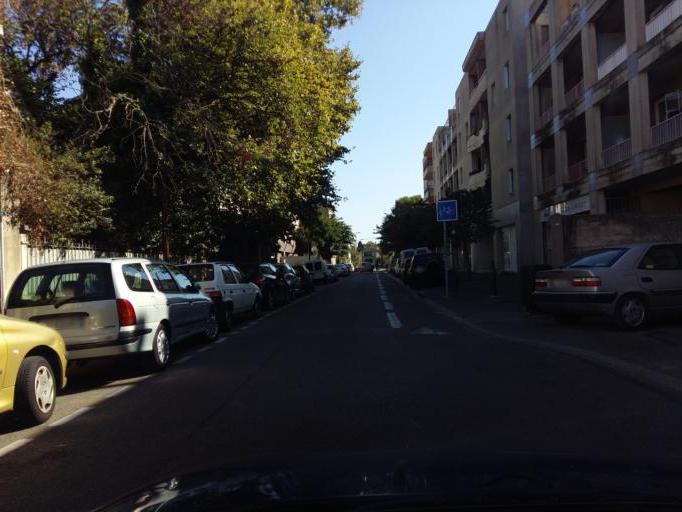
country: FR
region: Provence-Alpes-Cote d'Azur
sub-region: Departement du Vaucluse
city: Avignon
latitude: 43.9398
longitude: 4.8146
